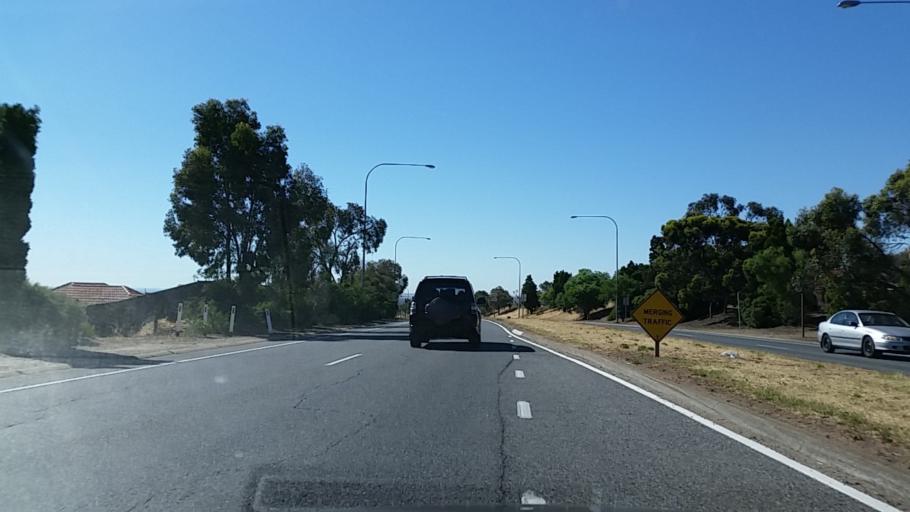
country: AU
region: South Australia
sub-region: Tea Tree Gully
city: Modbury
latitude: -34.8102
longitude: 138.6739
